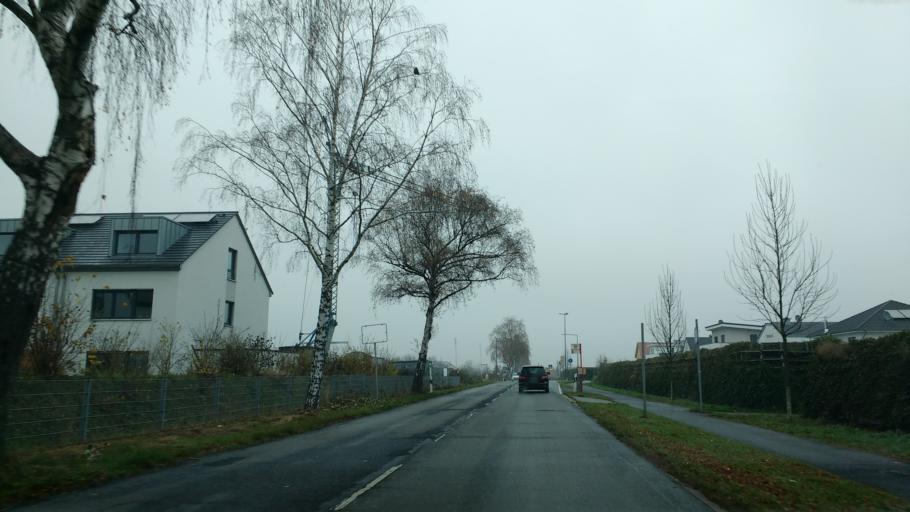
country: DE
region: North Rhine-Westphalia
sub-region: Regierungsbezirk Koln
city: Frechen
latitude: 50.9529
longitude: 6.8288
